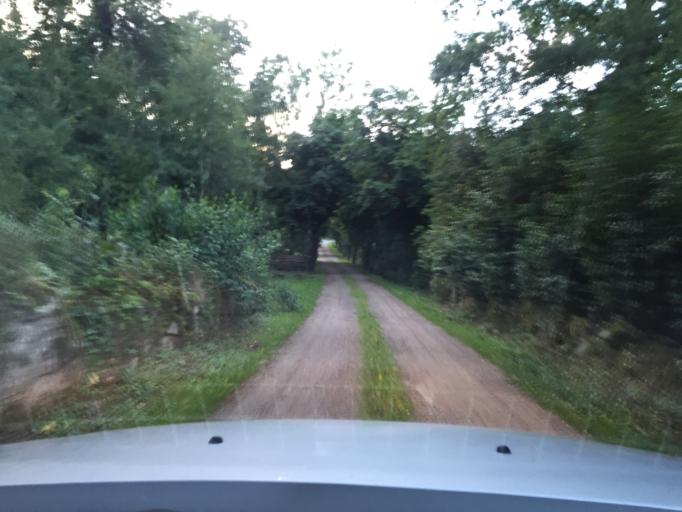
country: SE
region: Skane
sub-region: Hassleholms Kommun
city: Sosdala
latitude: 56.0373
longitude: 13.6972
